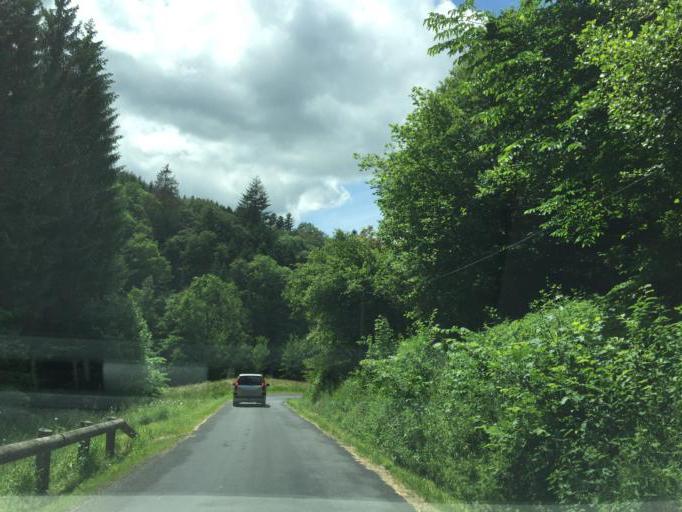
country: FR
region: Auvergne
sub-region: Departement du Puy-de-Dome
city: Ambert
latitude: 45.5395
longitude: 3.7960
